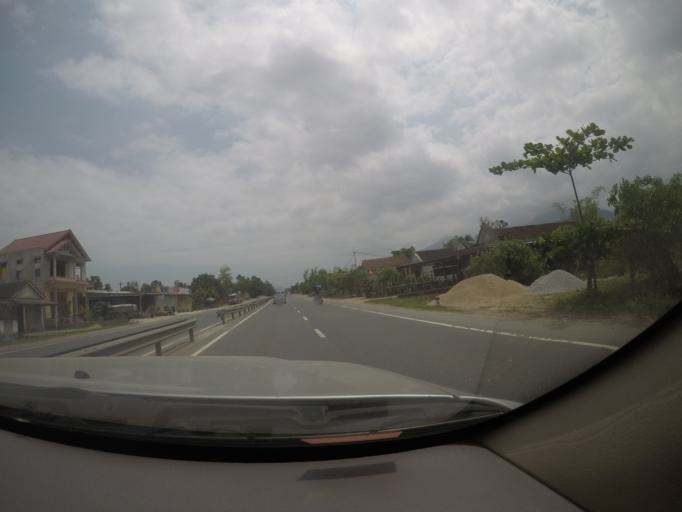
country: VN
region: Thua Thien-Hue
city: Phu Loc
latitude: 16.2725
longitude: 107.9434
